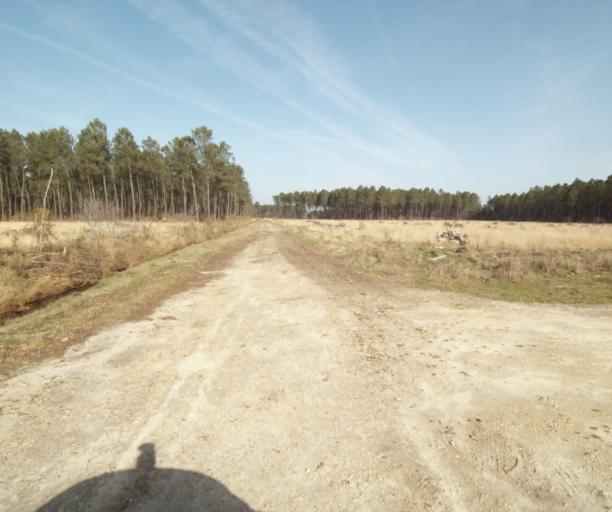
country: FR
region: Aquitaine
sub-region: Departement de la Gironde
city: Prechac
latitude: 44.2271
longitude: -0.2396
